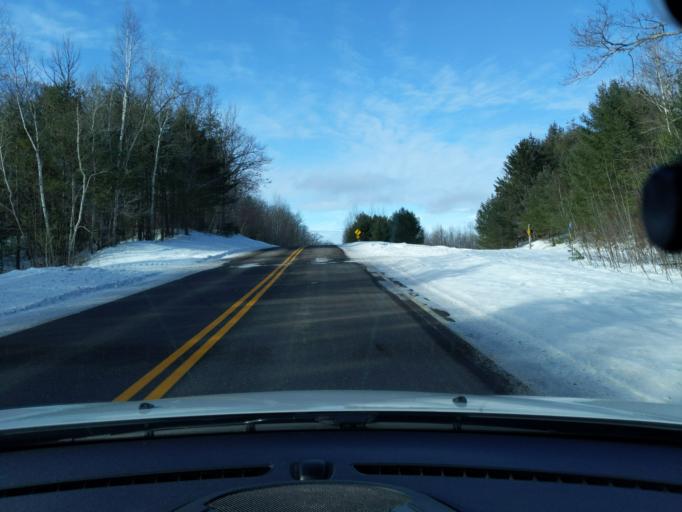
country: US
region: Wisconsin
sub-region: Sawyer County
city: Little Round Lake
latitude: 46.1160
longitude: -91.3343
